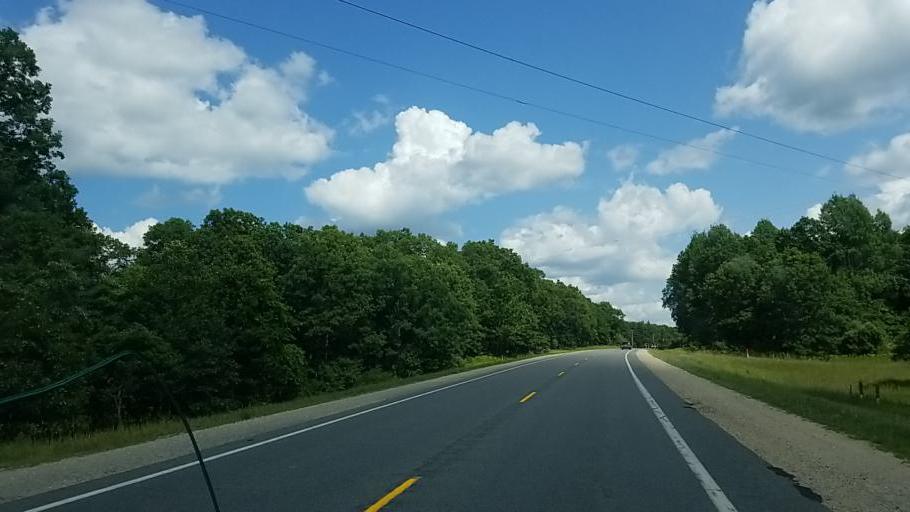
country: US
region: Michigan
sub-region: Newaygo County
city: Newaygo
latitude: 43.4061
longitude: -85.6813
